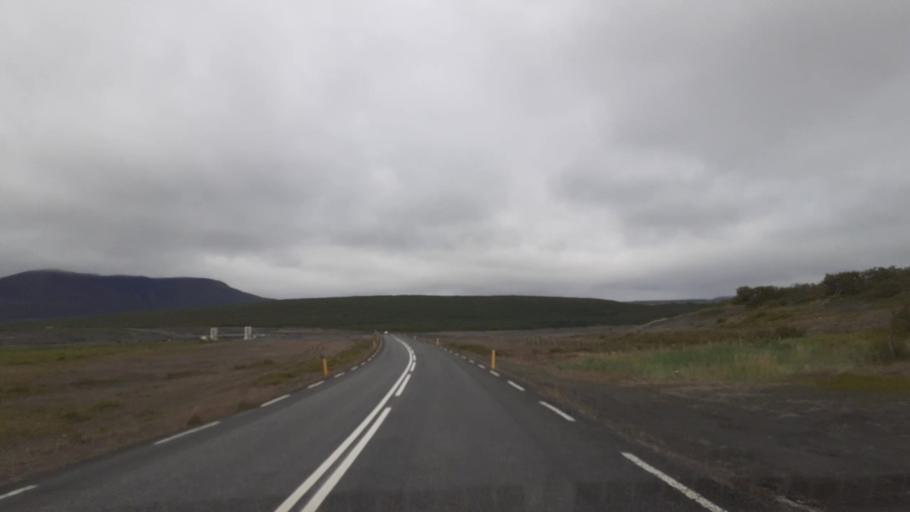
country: IS
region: Northeast
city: Husavik
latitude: 66.0306
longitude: -16.4654
